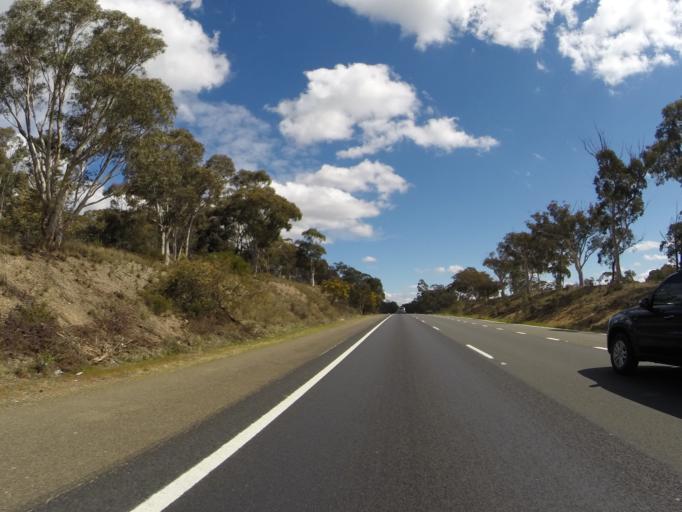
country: AU
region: New South Wales
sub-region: Goulburn Mulwaree
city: Goulburn
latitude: -34.7438
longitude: 149.8947
